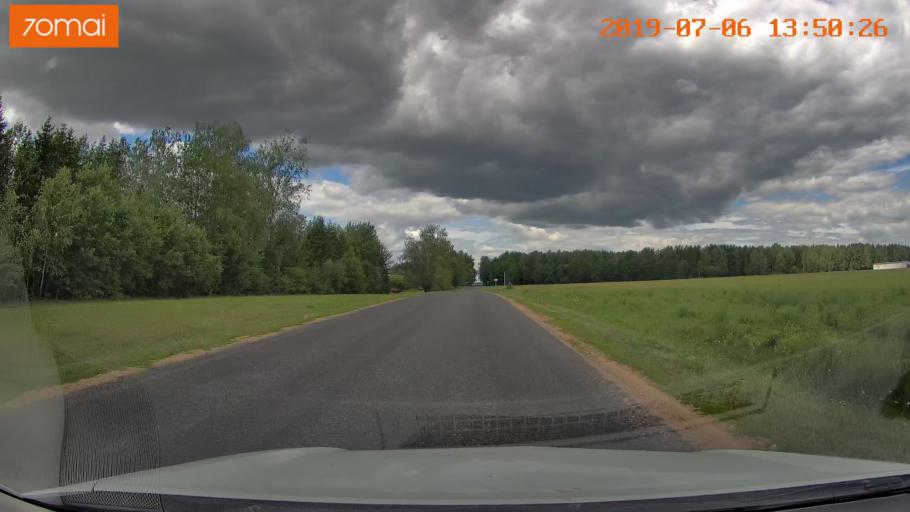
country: BY
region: Minsk
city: Ivyanyets
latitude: 53.6997
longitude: 26.8436
